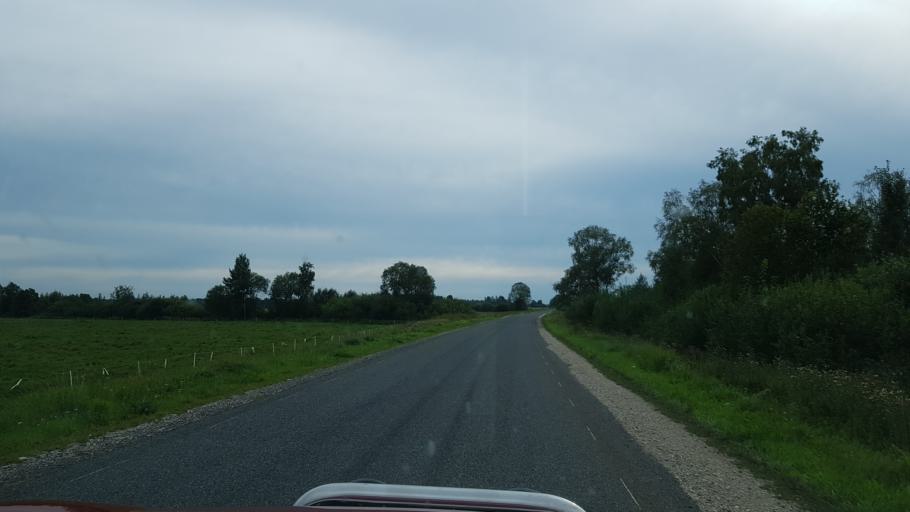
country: EE
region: Laeaene
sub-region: Lihula vald
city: Lihula
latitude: 58.8973
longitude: 23.8954
